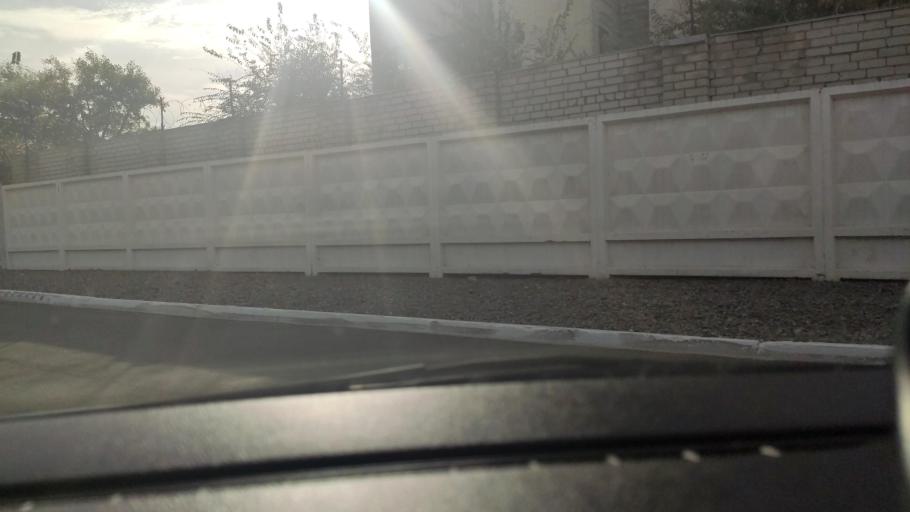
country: RU
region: Voronezj
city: Voronezh
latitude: 51.6553
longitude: 39.1767
